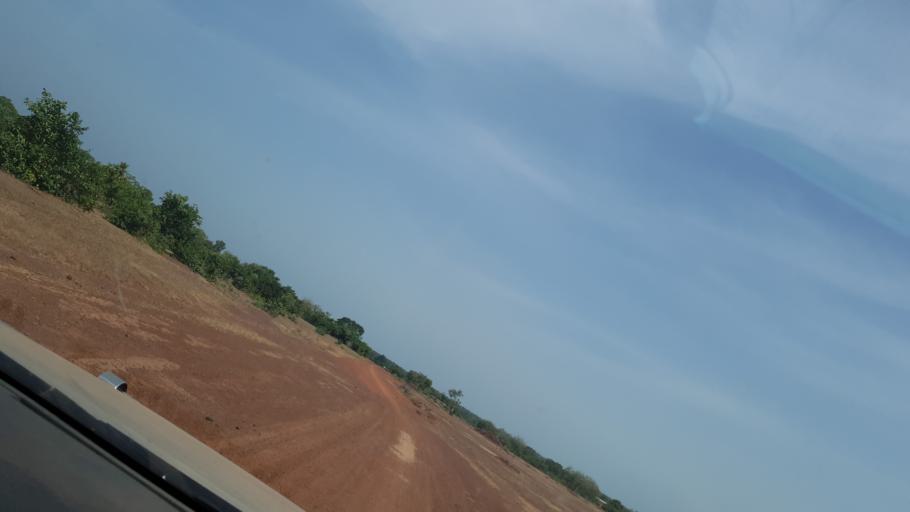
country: ML
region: Koulikoro
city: Dioila
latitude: 12.4703
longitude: -6.1860
